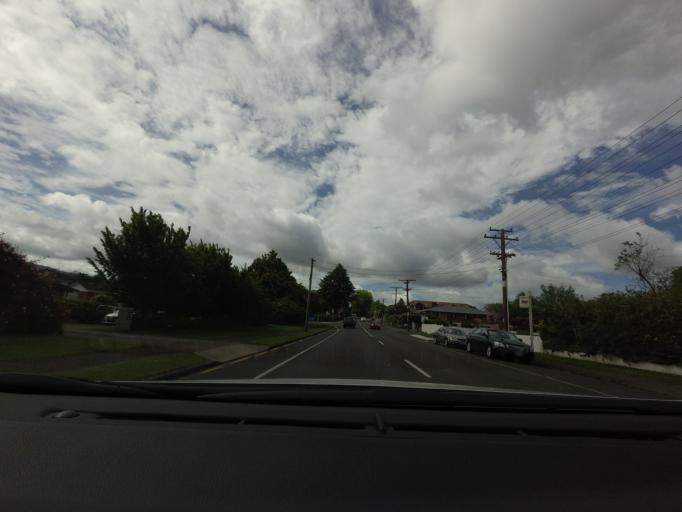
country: NZ
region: Bay of Plenty
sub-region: Rotorua District
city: Rotorua
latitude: -38.1559
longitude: 176.2412
